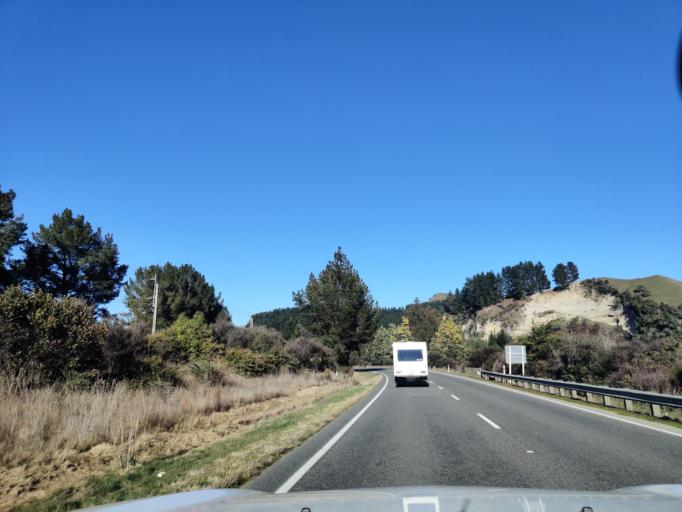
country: NZ
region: Manawatu-Wanganui
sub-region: Ruapehu District
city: Waiouru
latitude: -39.7542
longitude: 175.8311
